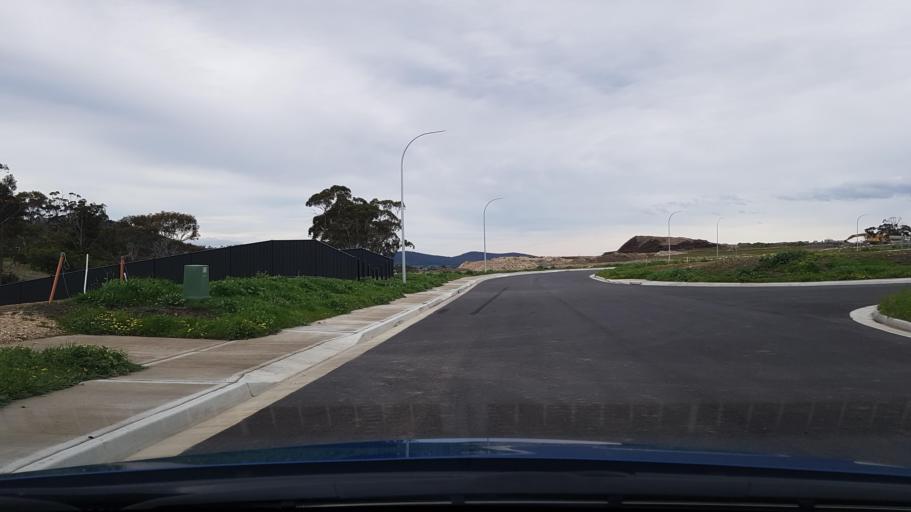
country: AU
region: Tasmania
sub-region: Clarence
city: Rokeby
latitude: -42.8771
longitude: 147.4321
